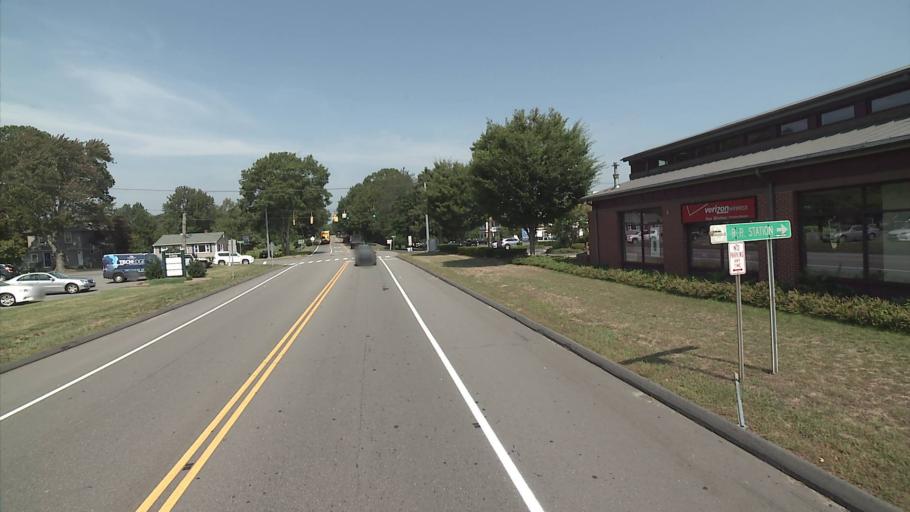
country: US
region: Connecticut
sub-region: New Haven County
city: Madison
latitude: 41.2812
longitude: -72.5992
